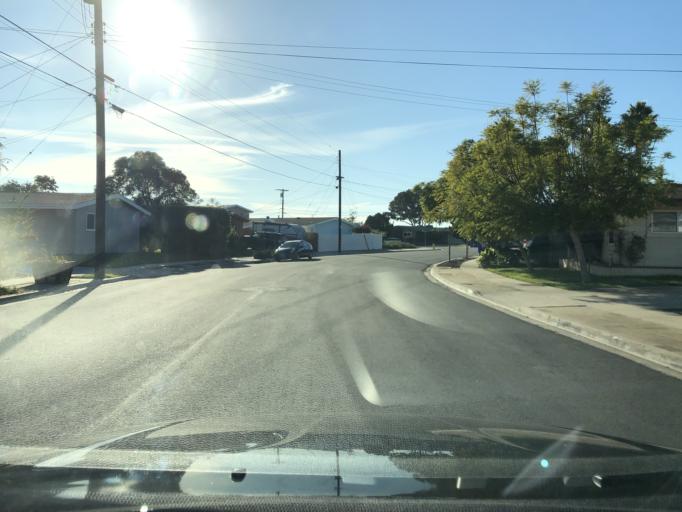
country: US
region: California
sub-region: San Diego County
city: La Jolla
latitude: 32.8194
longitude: -117.1976
